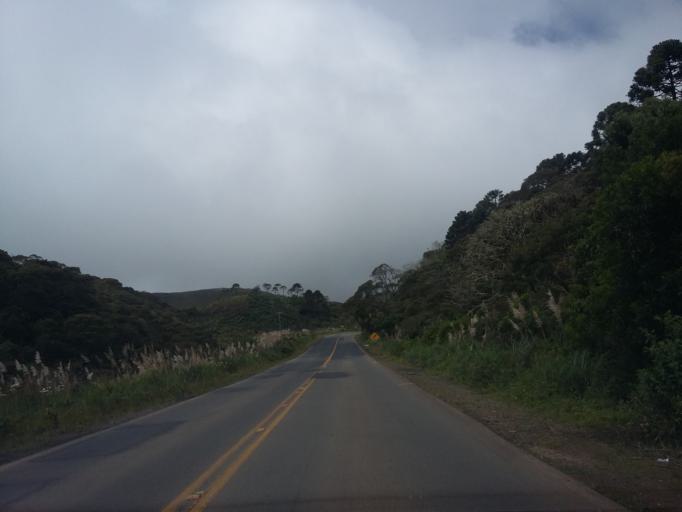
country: BR
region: Santa Catarina
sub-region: Lauro Muller
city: Lauro Muller
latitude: -28.3742
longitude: -49.5618
